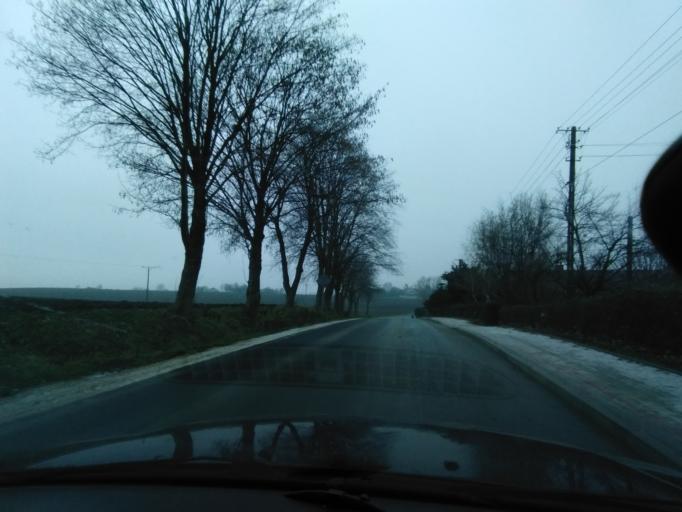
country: PL
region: Subcarpathian Voivodeship
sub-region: Powiat przeworski
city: Kanczuga
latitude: 50.0105
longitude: 22.4268
